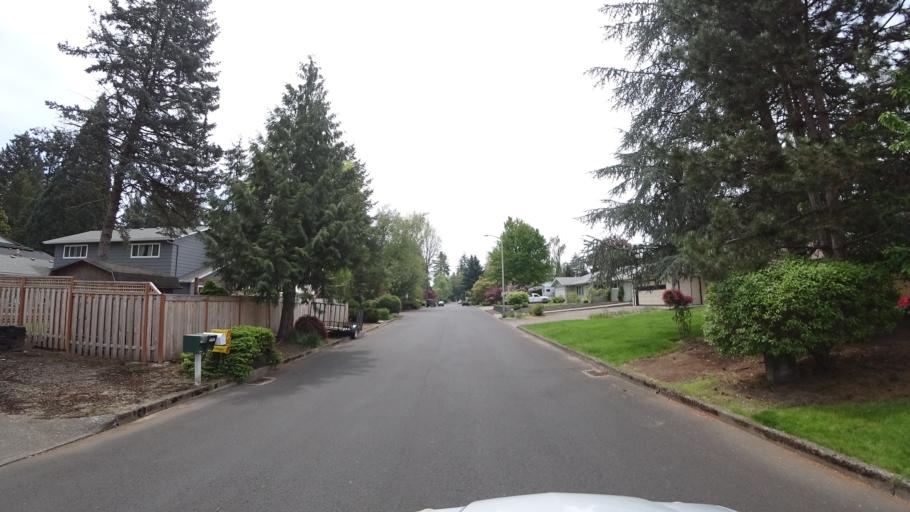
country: US
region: Oregon
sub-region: Washington County
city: Hillsboro
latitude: 45.5110
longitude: -122.9447
